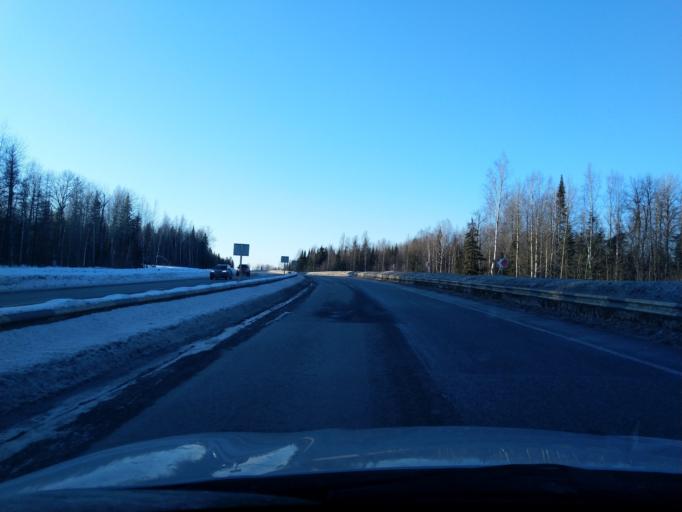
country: RU
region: Perm
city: Polazna
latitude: 58.3382
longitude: 56.4764
